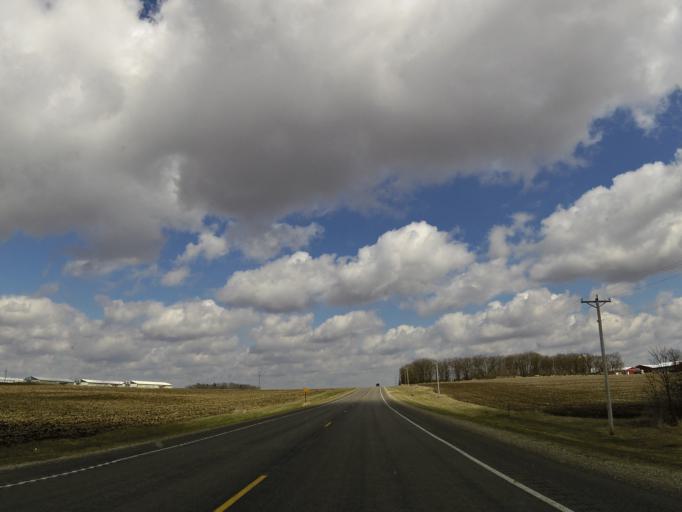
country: US
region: Minnesota
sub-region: Dodge County
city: Mantorville
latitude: 44.0800
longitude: -92.7428
